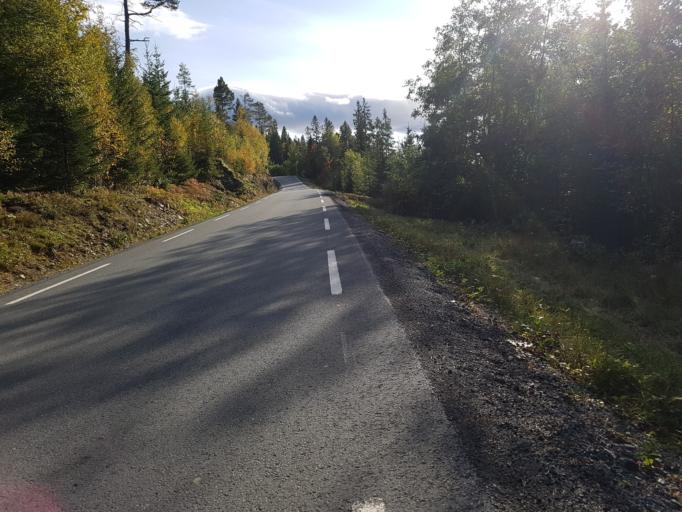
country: NO
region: Sor-Trondelag
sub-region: Malvik
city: Malvik
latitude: 63.3550
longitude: 10.6396
